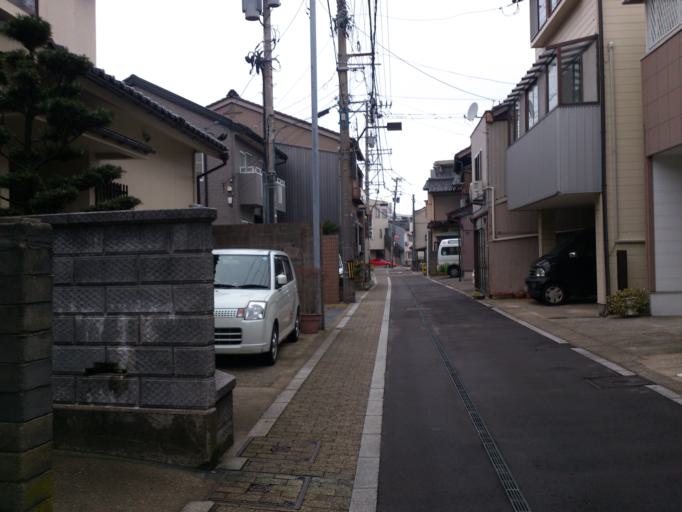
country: JP
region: Ishikawa
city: Kanazawa-shi
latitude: 36.5668
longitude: 136.6466
